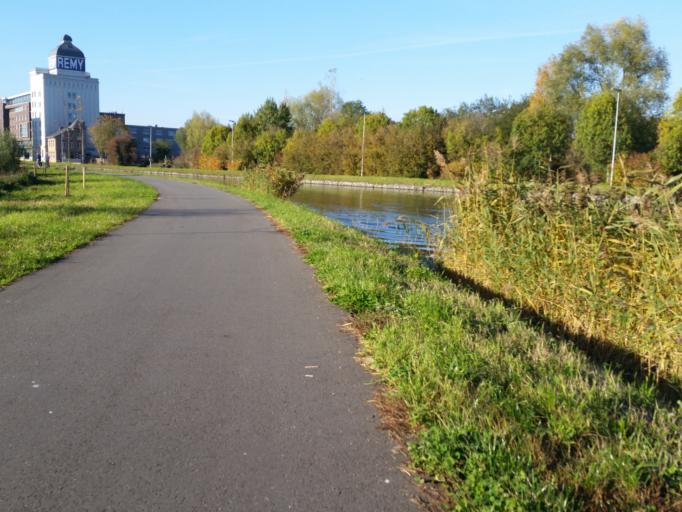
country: BE
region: Flanders
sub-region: Provincie Vlaams-Brabant
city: Herent
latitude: 50.9192
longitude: 4.7037
